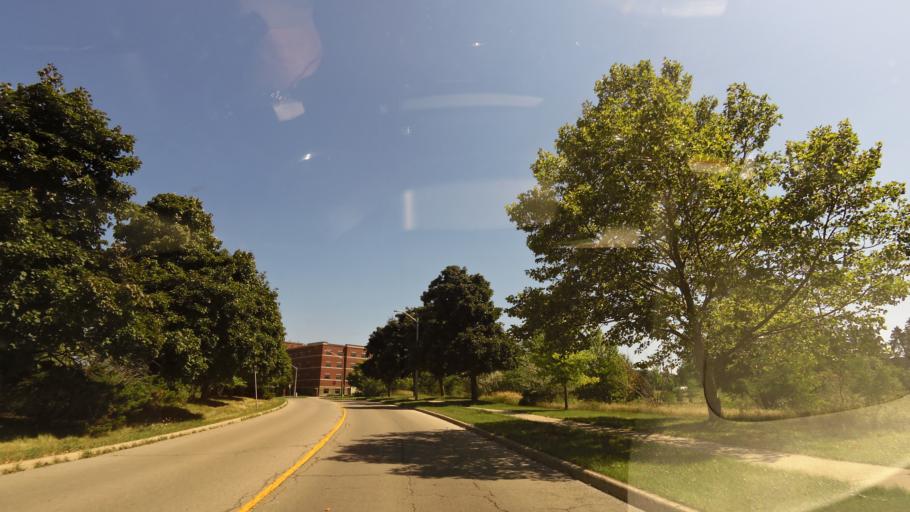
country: CA
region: Ontario
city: Hamilton
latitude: 43.2427
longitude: -79.9164
